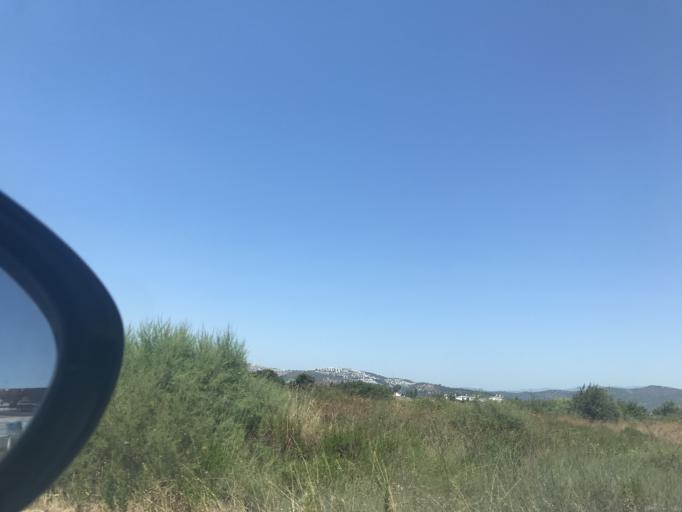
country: TR
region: Mugla
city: Kiulukioi
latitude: 37.1744
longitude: 27.6031
